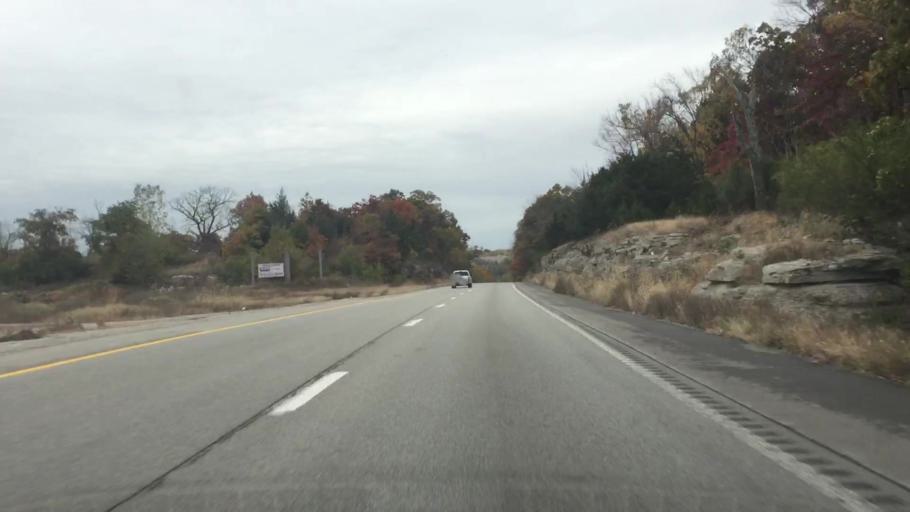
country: US
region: Missouri
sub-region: Jackson County
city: Lees Summit
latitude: 38.9555
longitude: -94.4194
